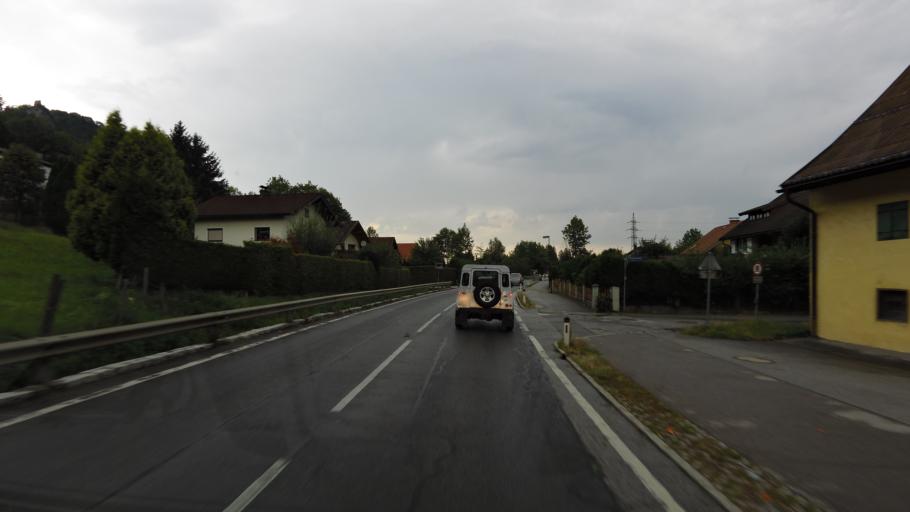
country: DE
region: Bavaria
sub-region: Upper Bavaria
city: Marktschellenberg
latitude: 47.7051
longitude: 13.0679
